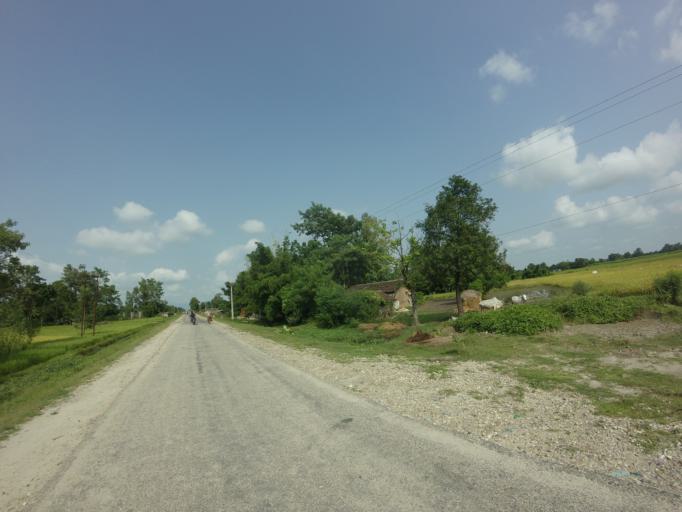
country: NP
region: Far Western
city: Tikapur
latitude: 28.4821
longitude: 81.0805
